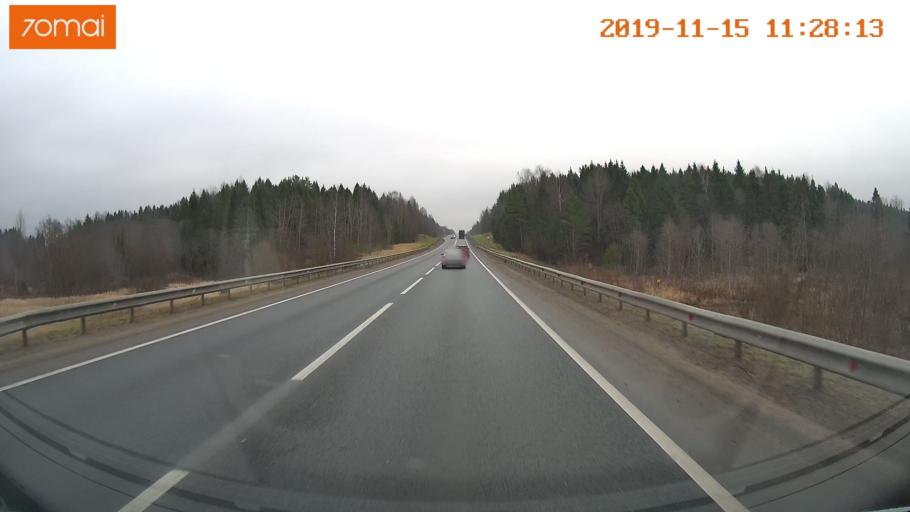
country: RU
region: Vologda
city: Molochnoye
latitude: 59.1718
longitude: 39.4832
